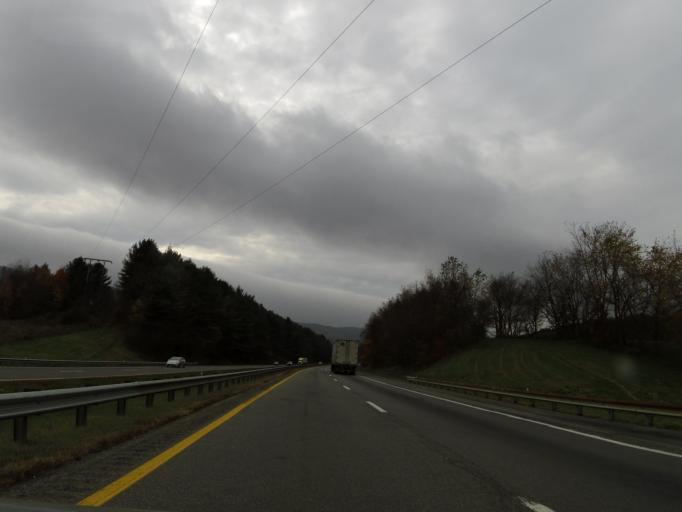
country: US
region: Virginia
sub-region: Bland County
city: Bland
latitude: 37.0665
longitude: -81.1271
